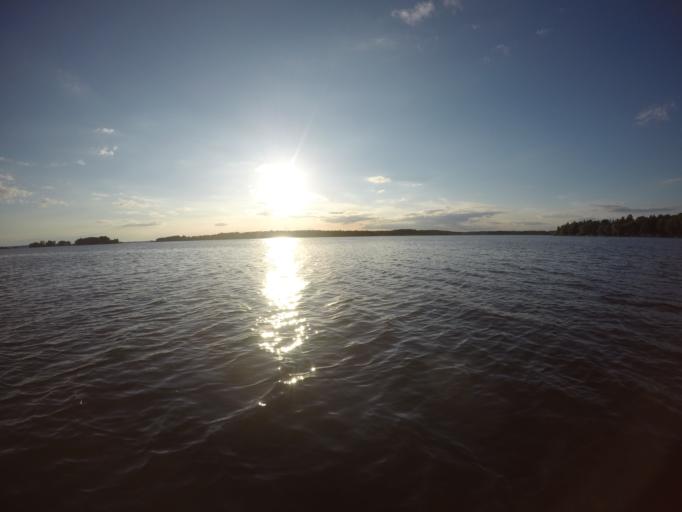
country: SE
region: Soedermanland
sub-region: Eskilstuna Kommun
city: Kvicksund
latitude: 59.4608
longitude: 16.2085
